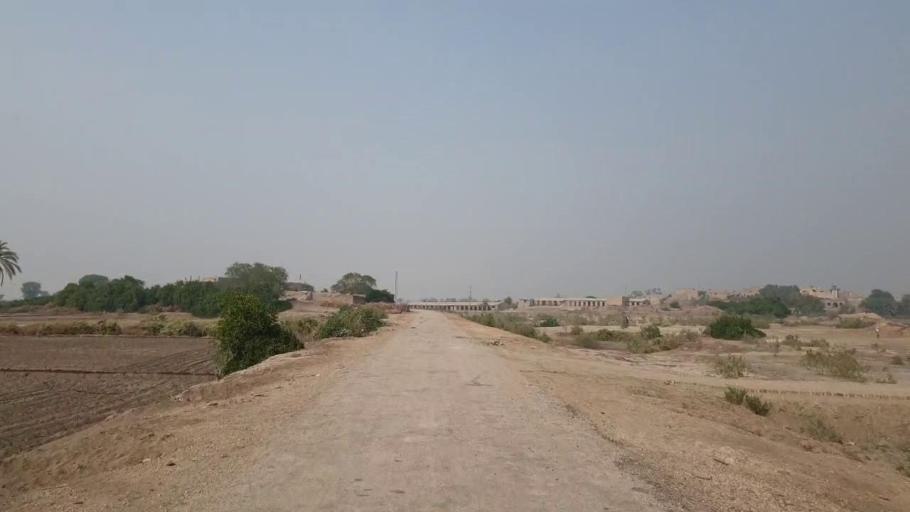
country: PK
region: Sindh
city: Bhan
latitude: 26.5036
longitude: 67.6923
